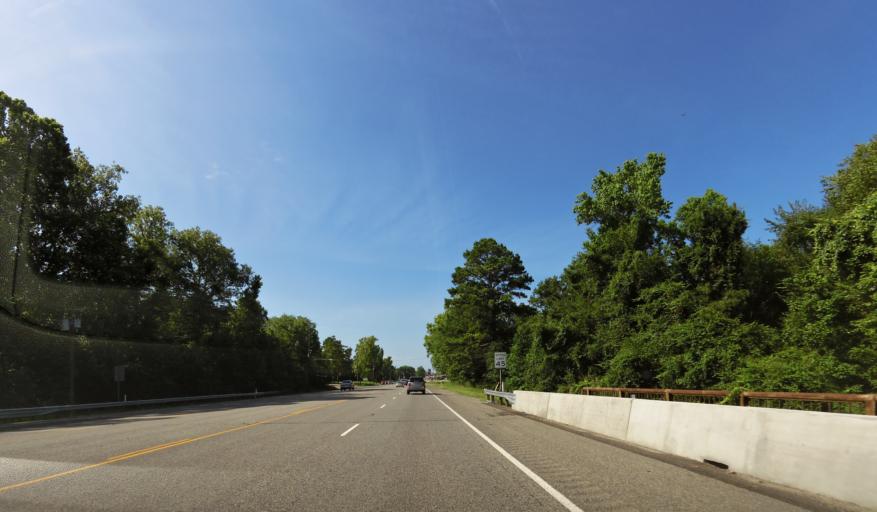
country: US
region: Texas
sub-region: Polk County
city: Corrigan
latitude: 31.0072
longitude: -94.8250
